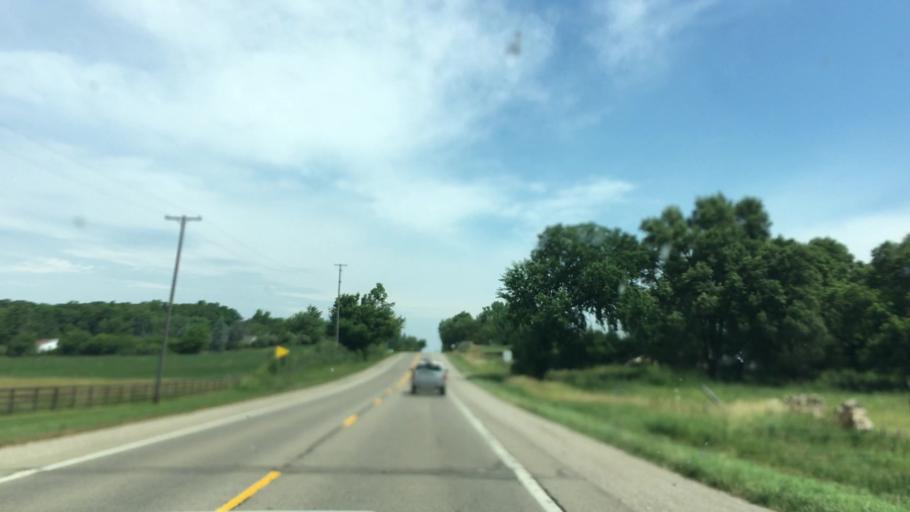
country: US
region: Michigan
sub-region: Lapeer County
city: Imlay City
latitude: 43.0702
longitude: -83.0750
